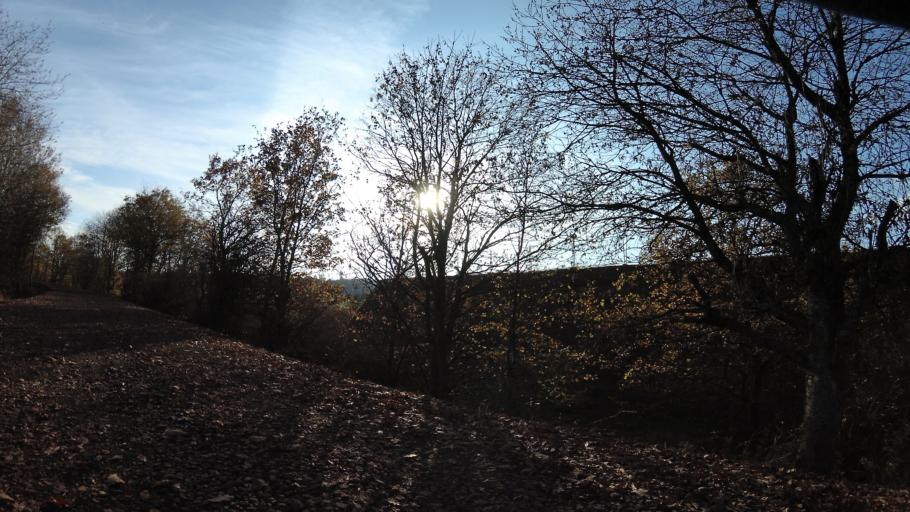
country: DE
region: Rheinland-Pfalz
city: Gimbweiler
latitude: 49.5549
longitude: 7.1758
